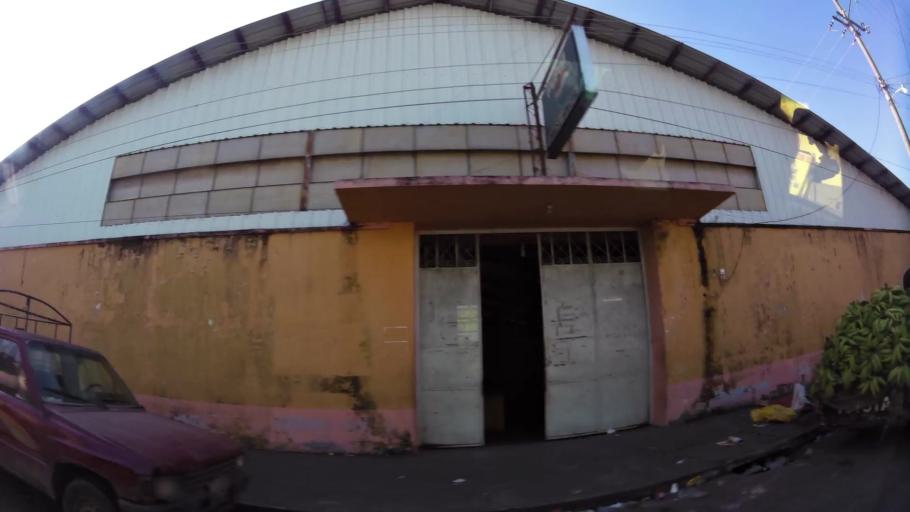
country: GT
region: Suchitepeque
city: Mazatenango
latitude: 14.5325
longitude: -91.5086
